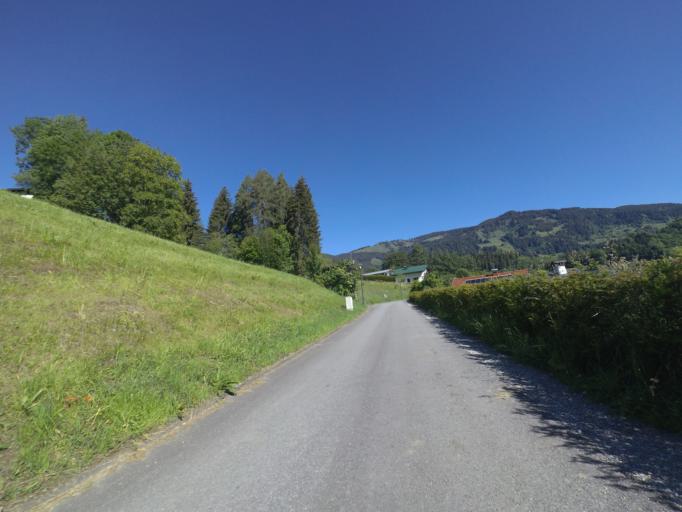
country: AT
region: Salzburg
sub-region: Politischer Bezirk Sankt Johann im Pongau
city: Goldegg
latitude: 47.3188
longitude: 13.0973
